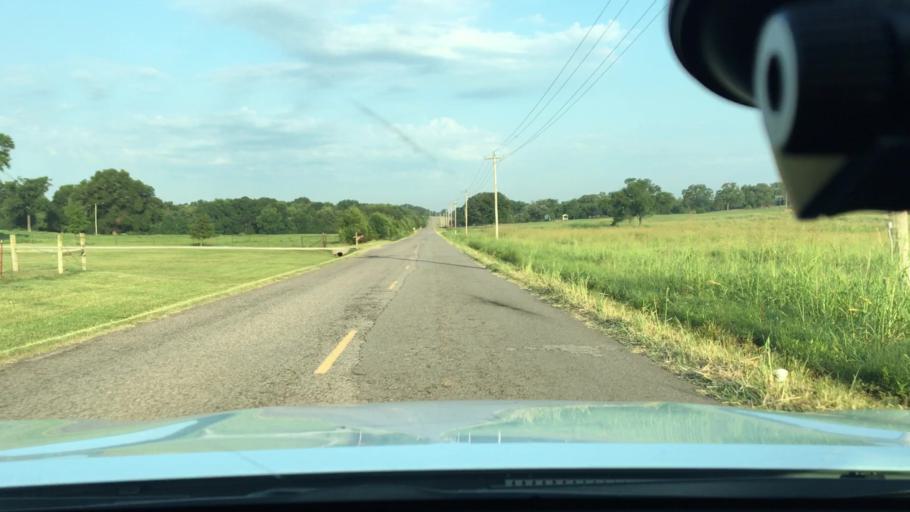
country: US
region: Arkansas
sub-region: Johnson County
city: Coal Hill
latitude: 35.3663
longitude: -93.6036
